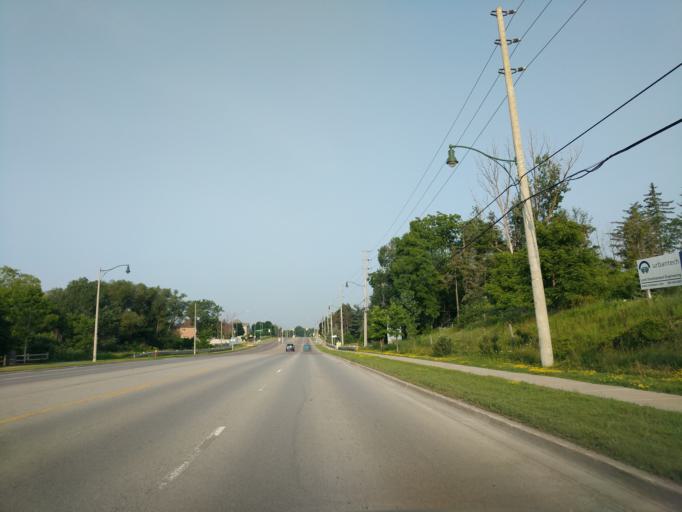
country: CA
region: Ontario
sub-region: York
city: Richmond Hill
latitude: 43.8953
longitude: -79.4103
